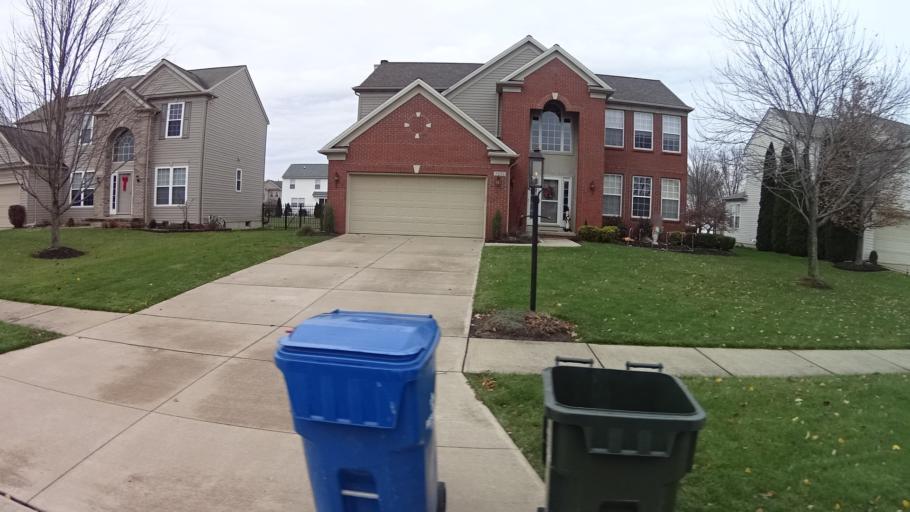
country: US
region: Ohio
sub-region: Lorain County
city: North Ridgeville
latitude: 41.3566
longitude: -82.0390
